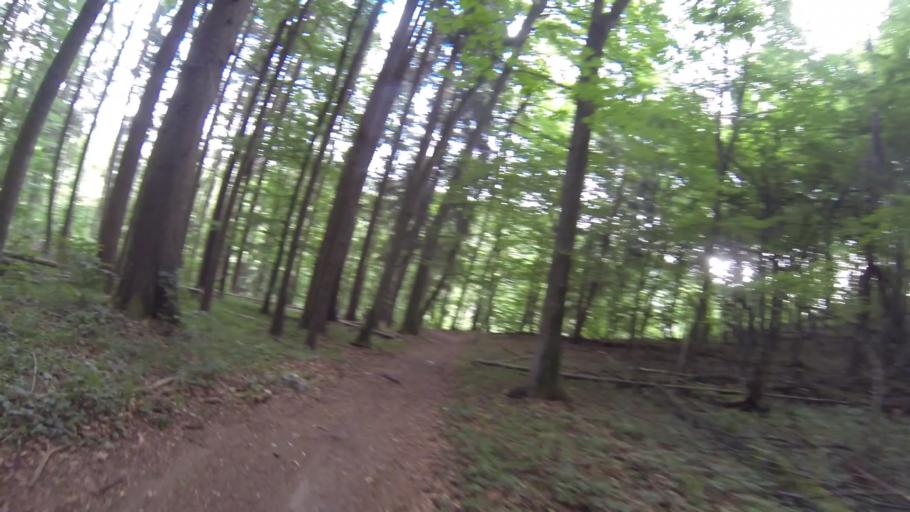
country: DE
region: Baden-Wuerttemberg
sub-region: Tuebingen Region
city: Blaubeuren
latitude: 48.4506
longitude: 9.8570
